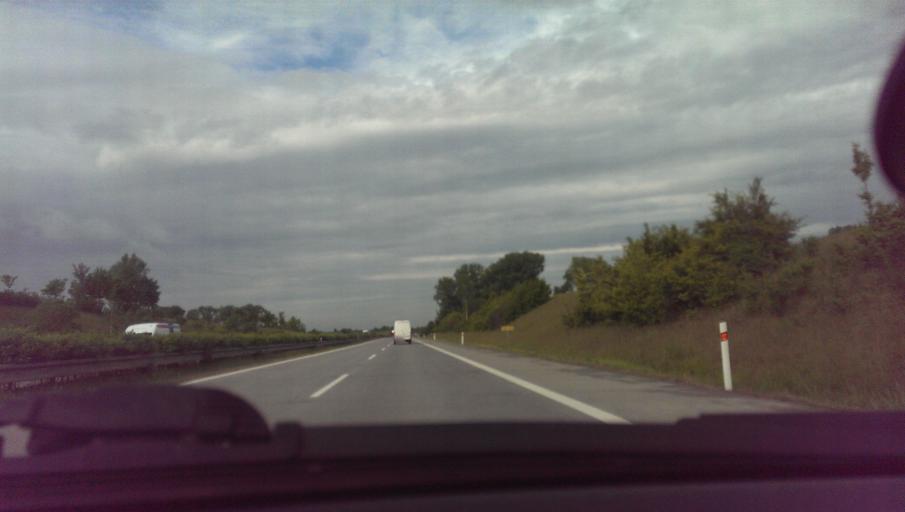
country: CZ
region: Olomoucky
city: Nezamyslice
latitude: 49.3140
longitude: 17.1544
